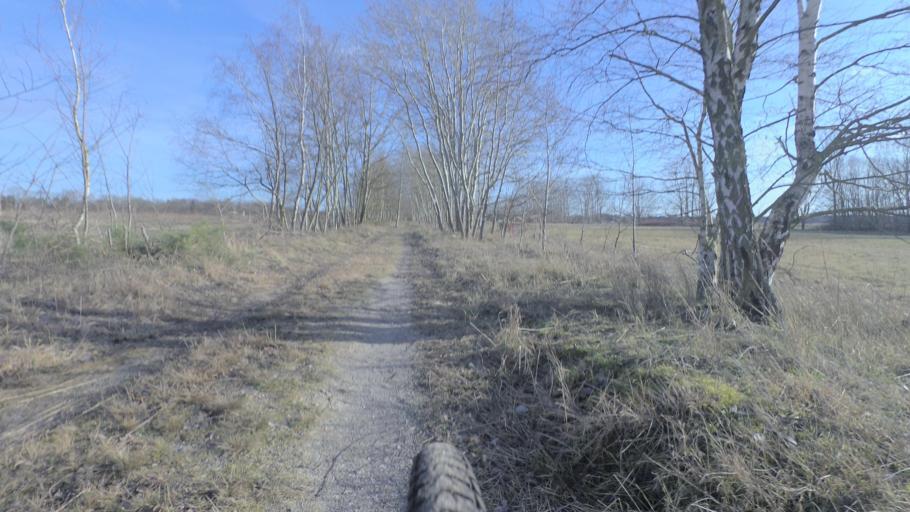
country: DE
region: Brandenburg
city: Ludwigsfelde
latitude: 52.2473
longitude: 13.2833
